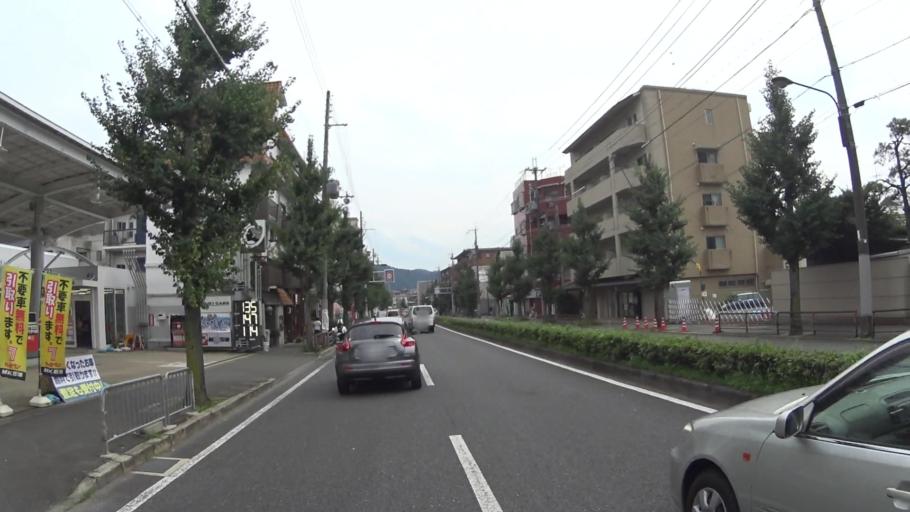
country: JP
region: Kyoto
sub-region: Kyoto-shi
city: Kamigyo-ku
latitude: 35.0248
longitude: 135.7918
